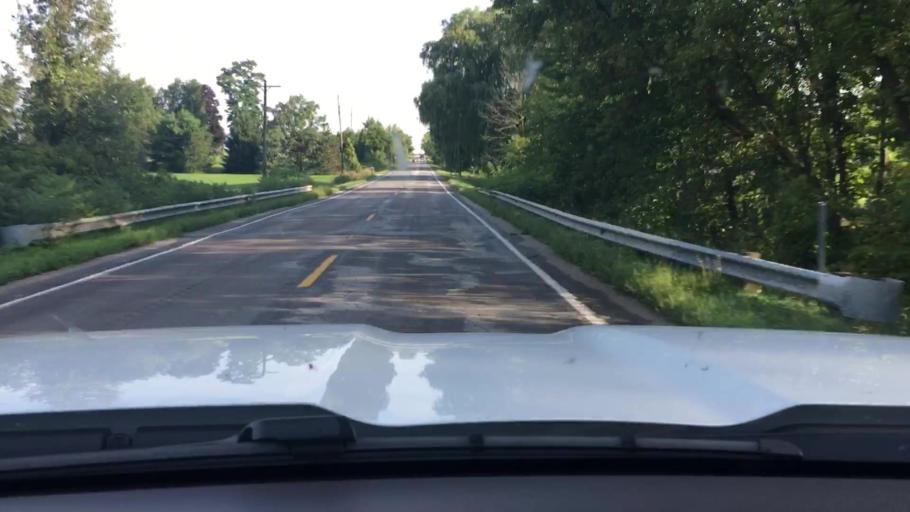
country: US
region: Michigan
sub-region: Kent County
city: Kent City
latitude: 43.2072
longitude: -85.7709
